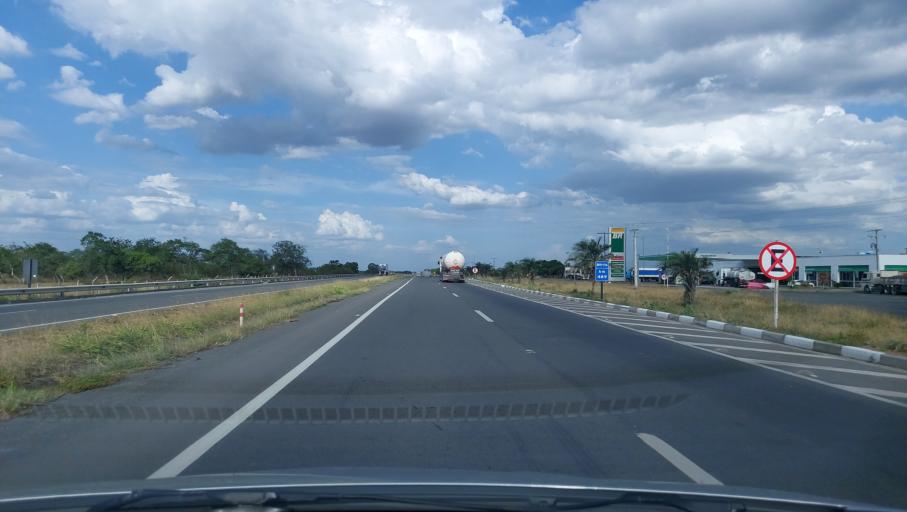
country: BR
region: Bahia
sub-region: Castro Alves
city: Castro Alves
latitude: -12.5603
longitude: -39.4725
